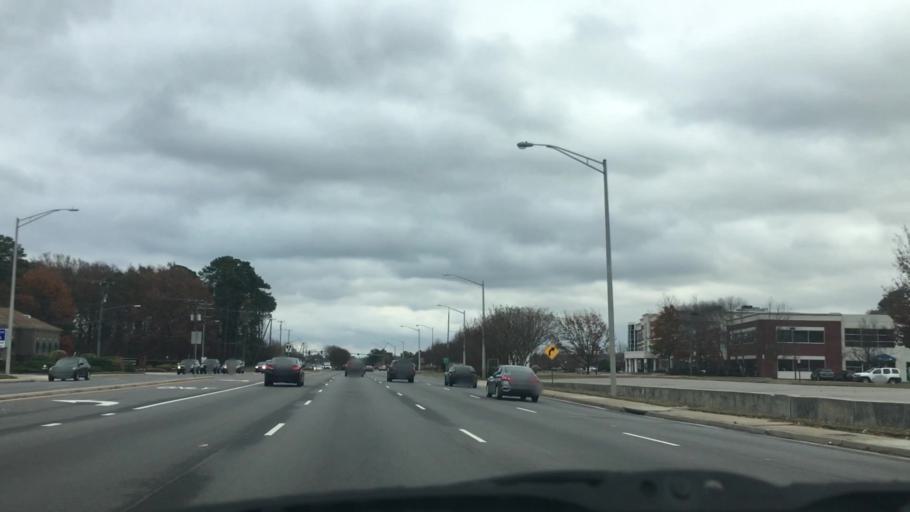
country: US
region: Virginia
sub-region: City of Chesapeake
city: Chesapeake
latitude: 36.8253
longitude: -76.1296
